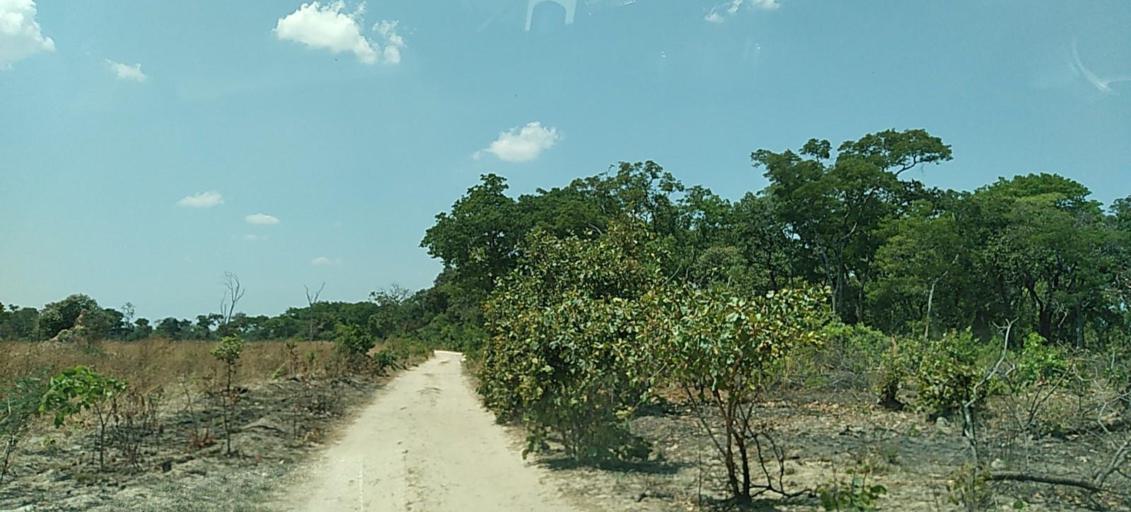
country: ZM
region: Central
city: Kapiri Mposhi
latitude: -13.6606
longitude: 28.4912
